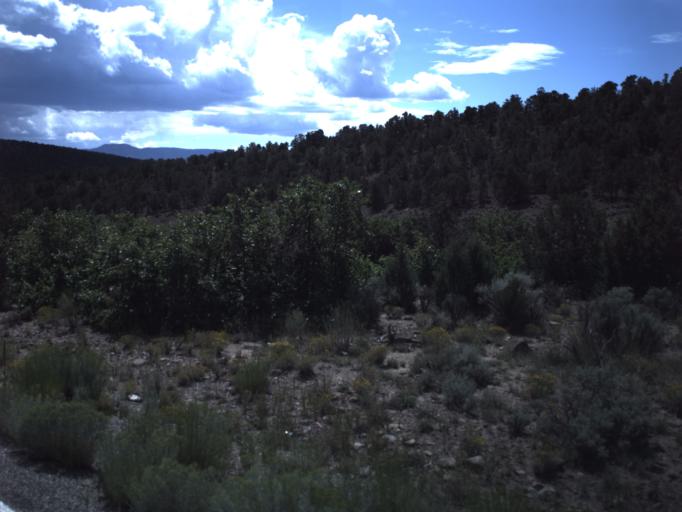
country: US
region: Utah
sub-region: Piute County
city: Junction
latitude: 38.2589
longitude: -112.2895
